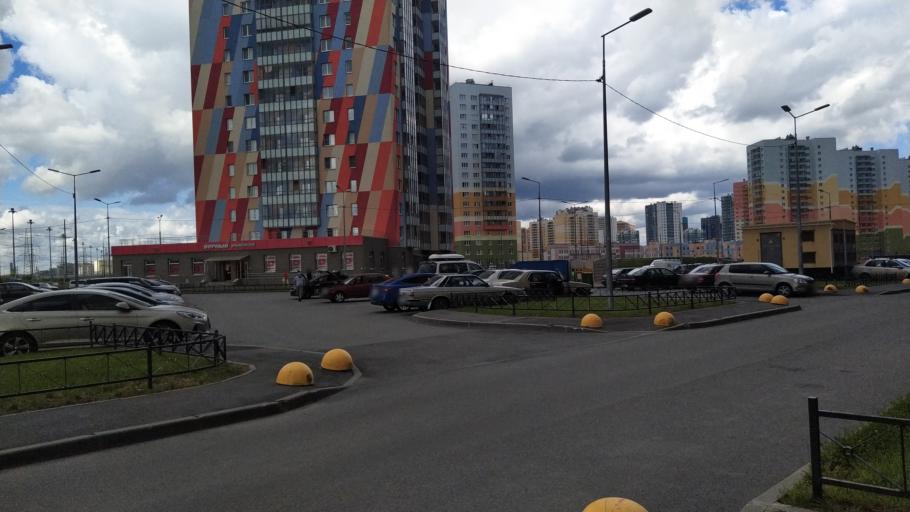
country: RU
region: Leningrad
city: Murino
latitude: 60.0276
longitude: 30.4528
